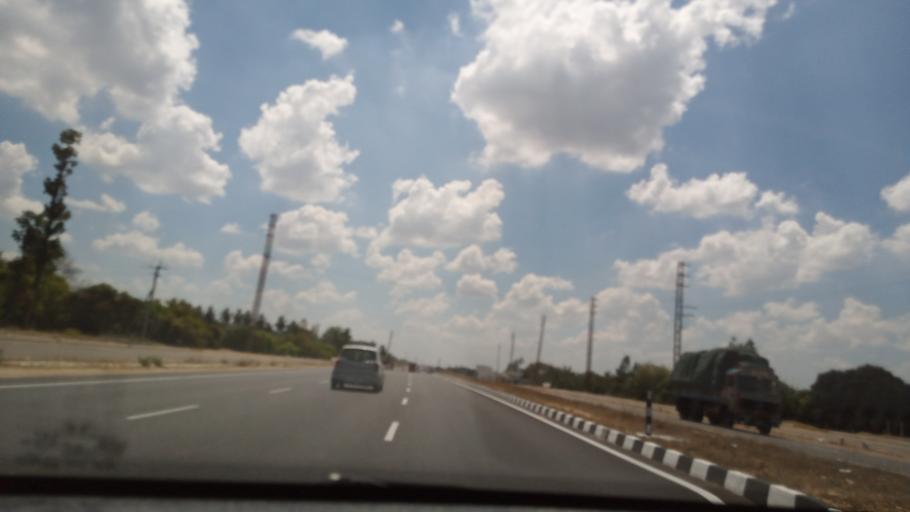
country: IN
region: Andhra Pradesh
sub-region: Chittoor
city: Pakala
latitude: 13.4613
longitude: 79.1705
